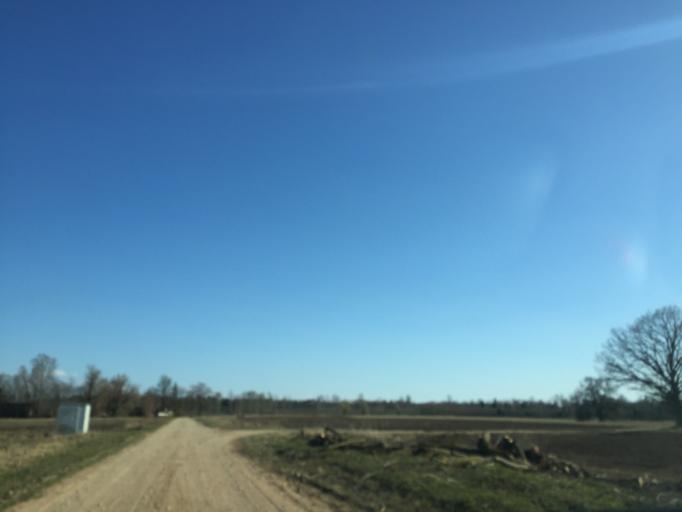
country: EE
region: Valgamaa
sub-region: Torva linn
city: Torva
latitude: 58.2386
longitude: 25.9283
